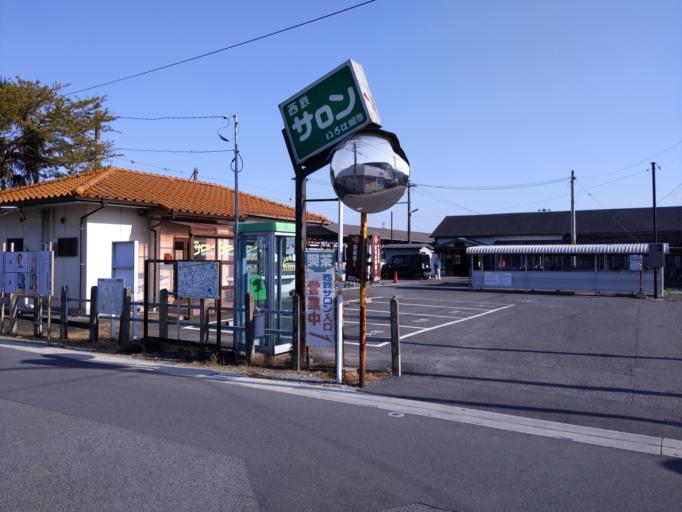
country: JP
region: Gifu
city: Godo
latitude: 35.3878
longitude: 136.5818
